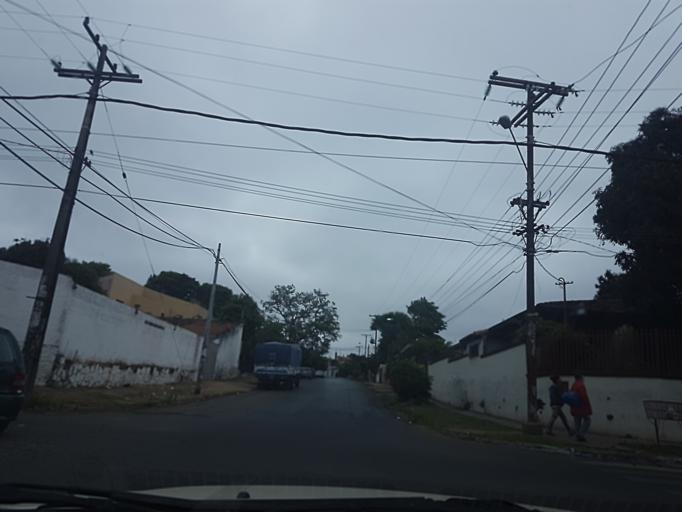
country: PY
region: Central
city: Lambare
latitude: -25.3219
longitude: -57.5974
